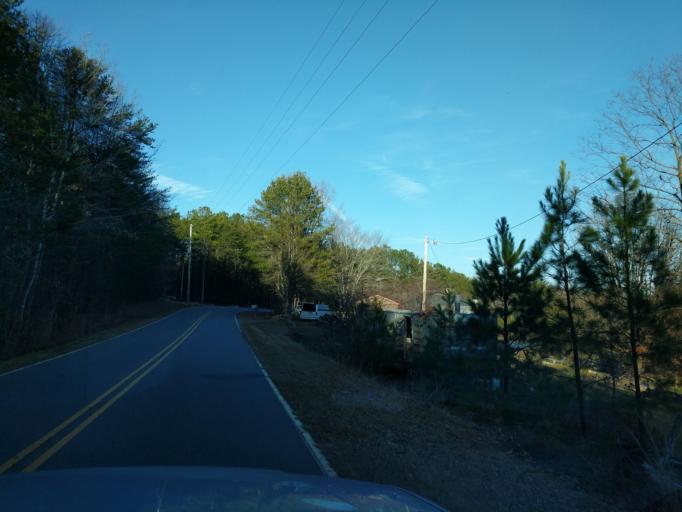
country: US
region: North Carolina
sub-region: Rutherford County
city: Lake Lure
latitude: 35.4040
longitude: -82.1767
